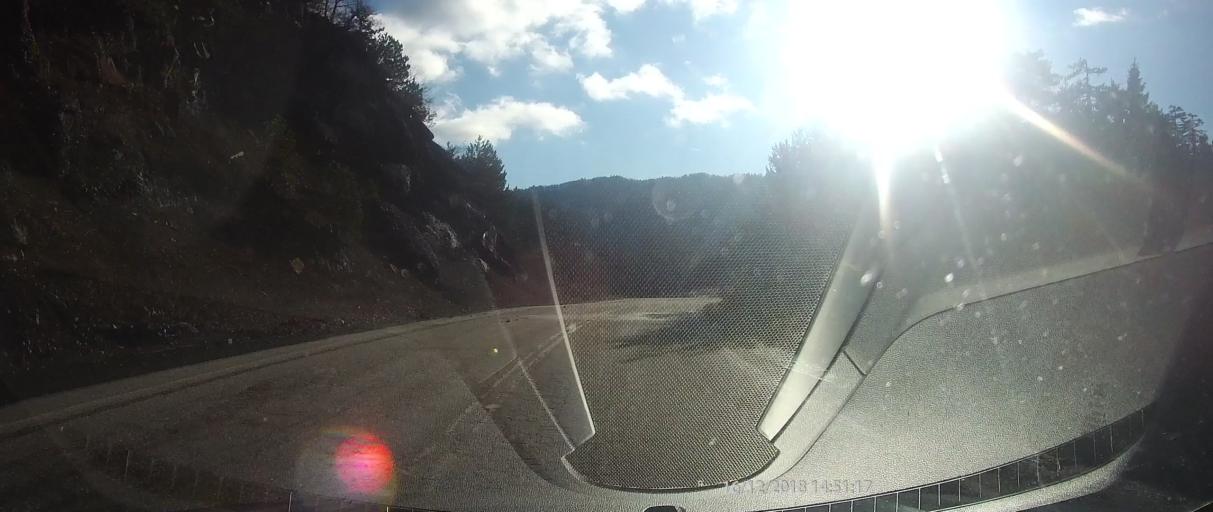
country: GR
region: West Macedonia
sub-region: Nomos Kastorias
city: Nestorio
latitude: 40.2053
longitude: 21.0737
